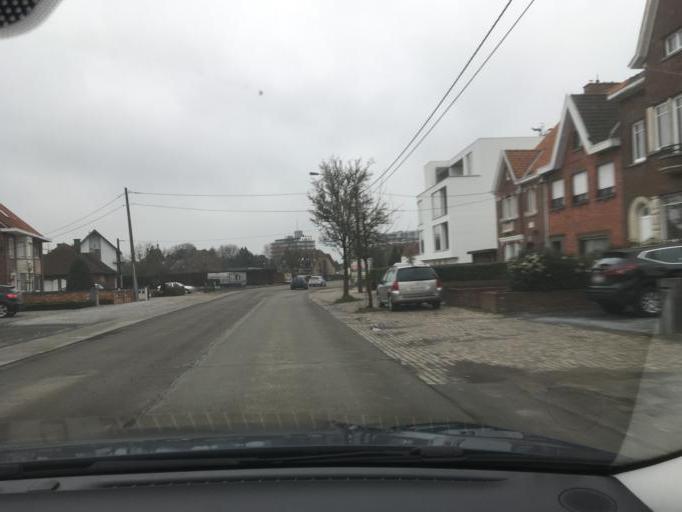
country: BE
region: Flanders
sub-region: Provincie West-Vlaanderen
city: Waregem
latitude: 50.8802
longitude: 3.4387
